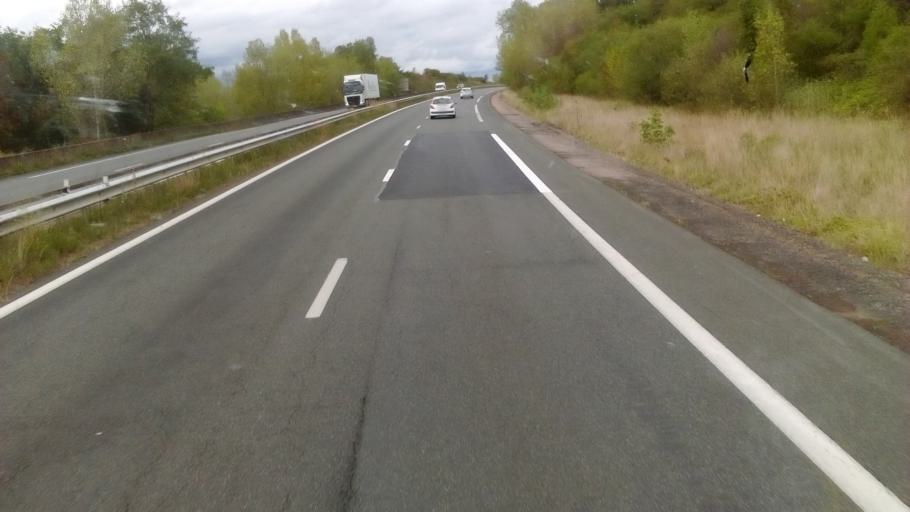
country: FR
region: Rhone-Alpes
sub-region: Departement de la Loire
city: Commelle-Vernay
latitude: 45.9801
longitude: 4.1207
